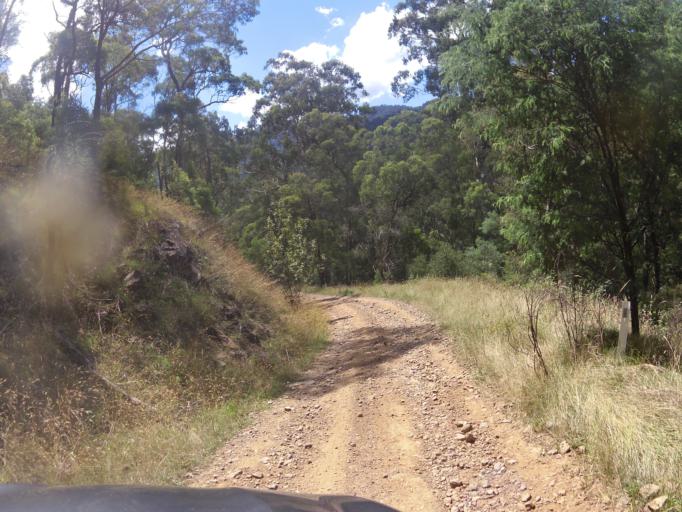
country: AU
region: Victoria
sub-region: Alpine
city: Mount Beauty
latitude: -36.7863
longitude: 147.0767
